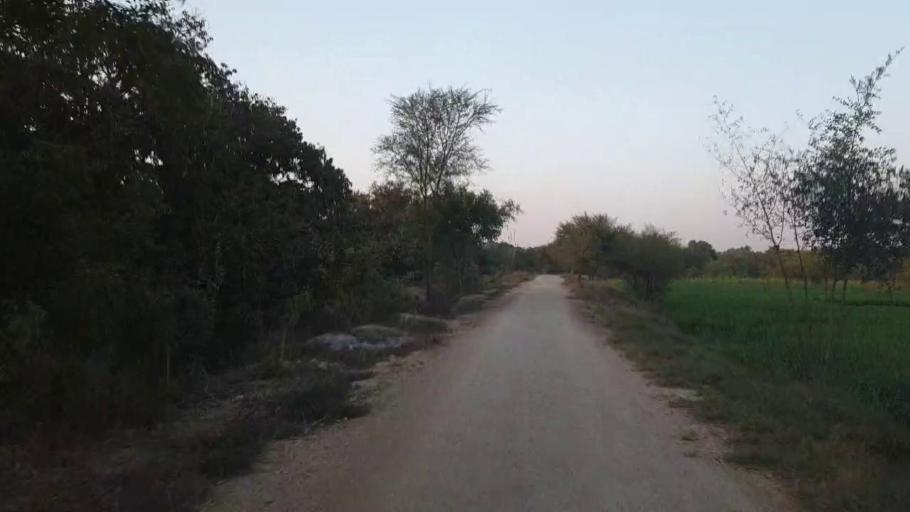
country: PK
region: Sindh
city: Chambar
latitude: 25.4161
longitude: 68.8659
